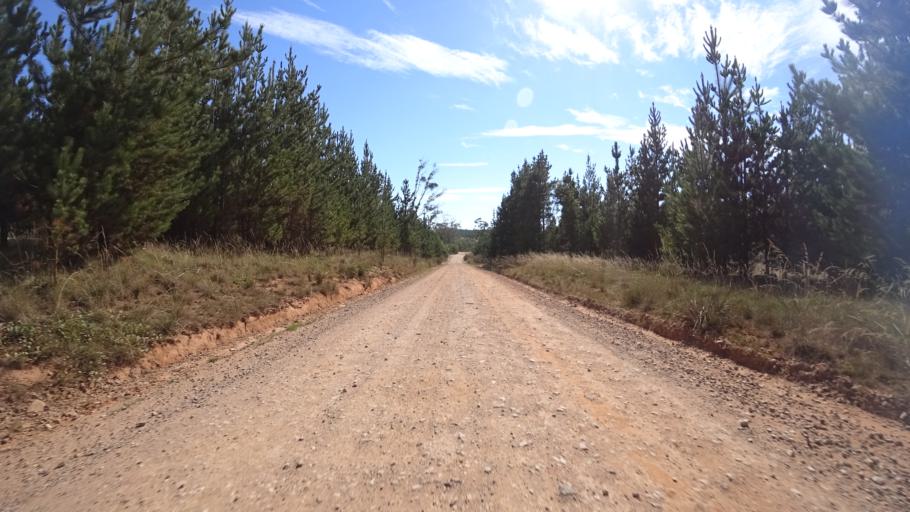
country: AU
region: New South Wales
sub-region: Lithgow
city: Lithgow
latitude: -33.3590
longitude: 150.2508
